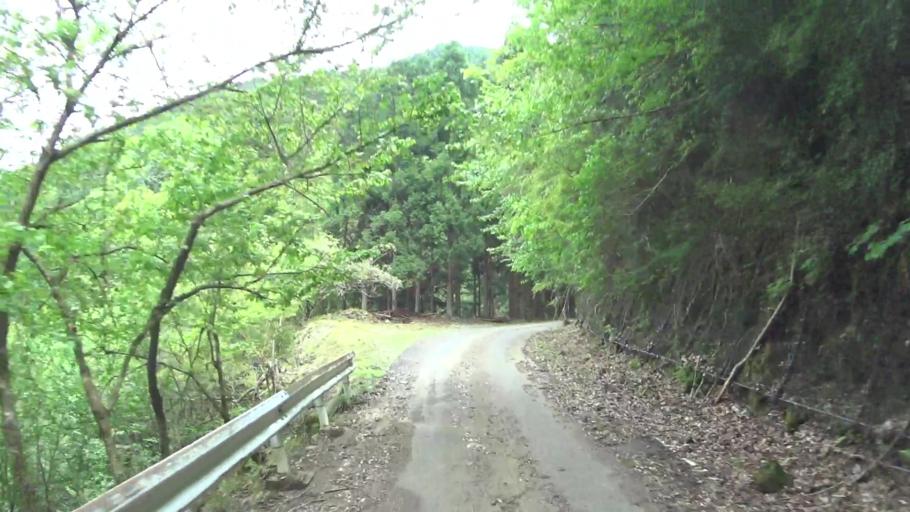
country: JP
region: Kyoto
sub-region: Kyoto-shi
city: Kamigyo-ku
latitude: 35.1801
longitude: 135.7038
